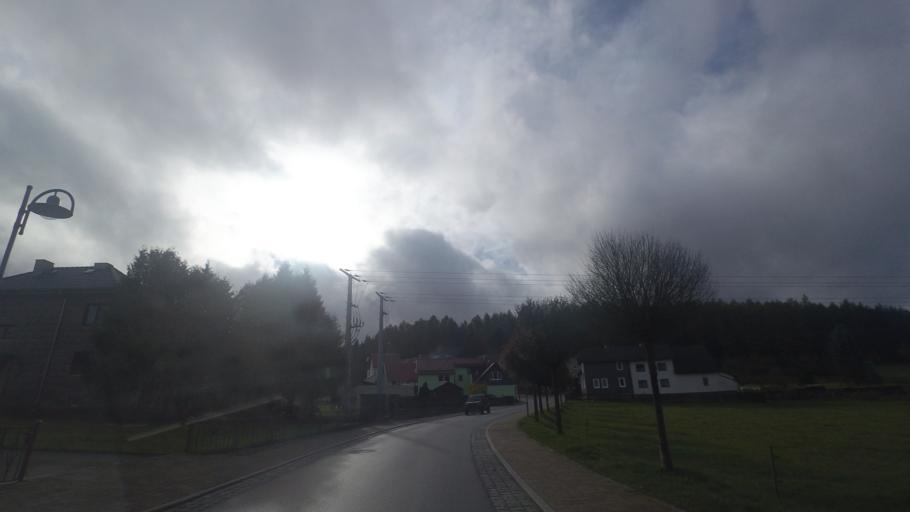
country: DE
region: Thuringia
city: Schleusingen
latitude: 50.4827
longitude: 10.8290
